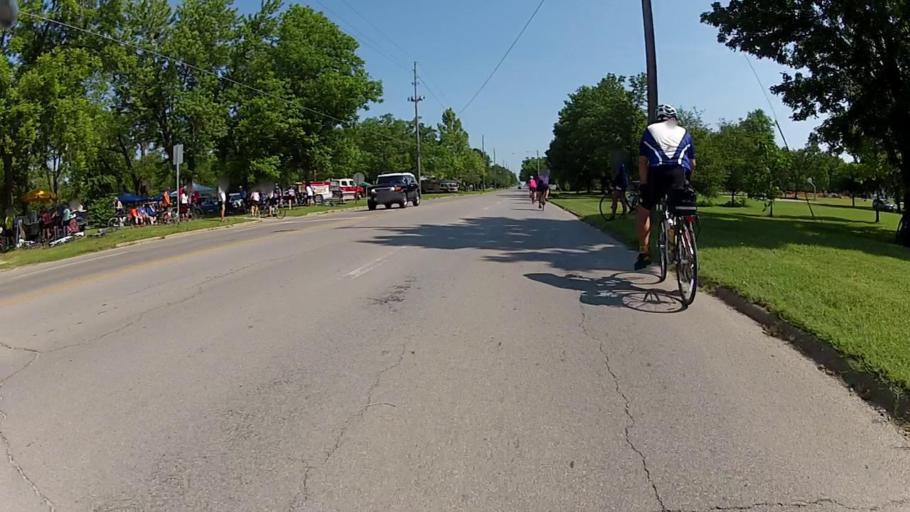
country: US
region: Kansas
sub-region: Montgomery County
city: Independence
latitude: 37.2167
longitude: -95.7108
